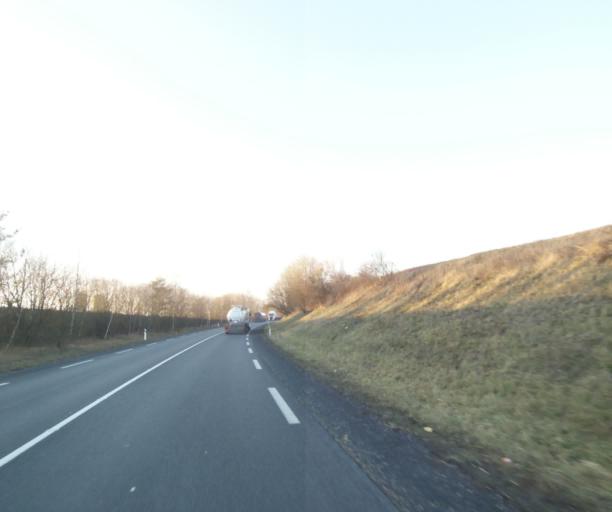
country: FR
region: Champagne-Ardenne
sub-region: Departement de la Haute-Marne
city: Bienville
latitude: 48.5465
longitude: 5.0690
